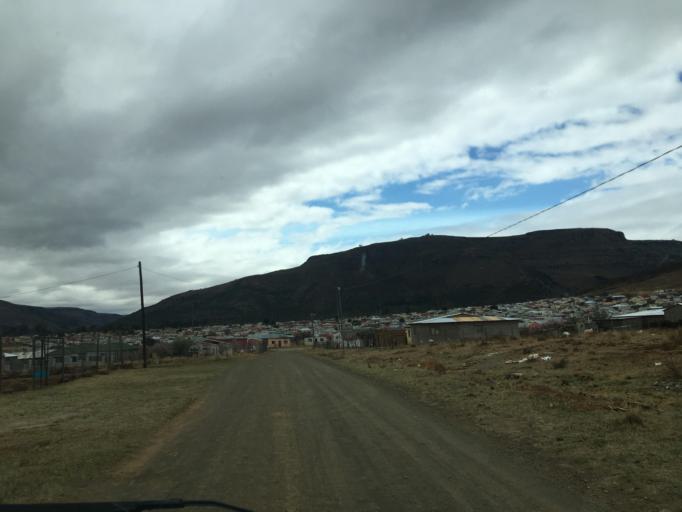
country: ZA
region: Eastern Cape
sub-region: Chris Hani District Municipality
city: Cala
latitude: -31.5397
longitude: 27.6982
